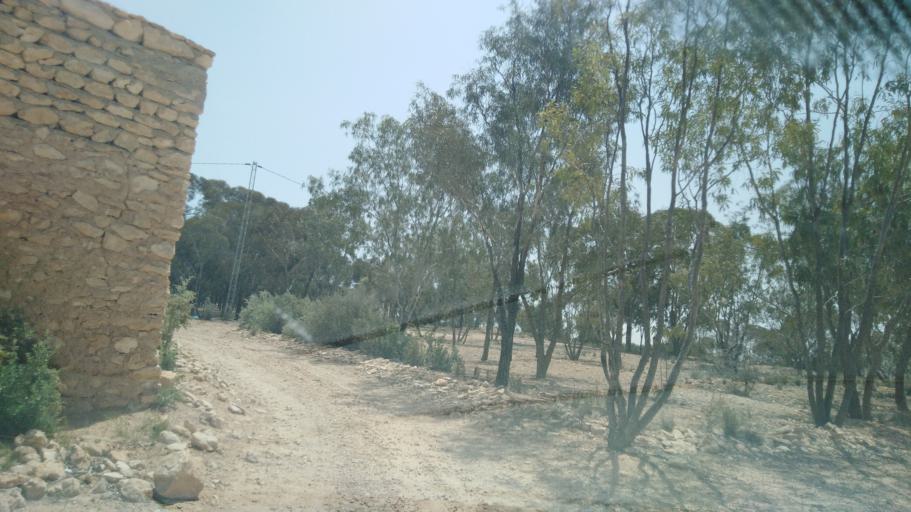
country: TN
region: Safaqis
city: Sfax
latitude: 34.7239
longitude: 10.5724
